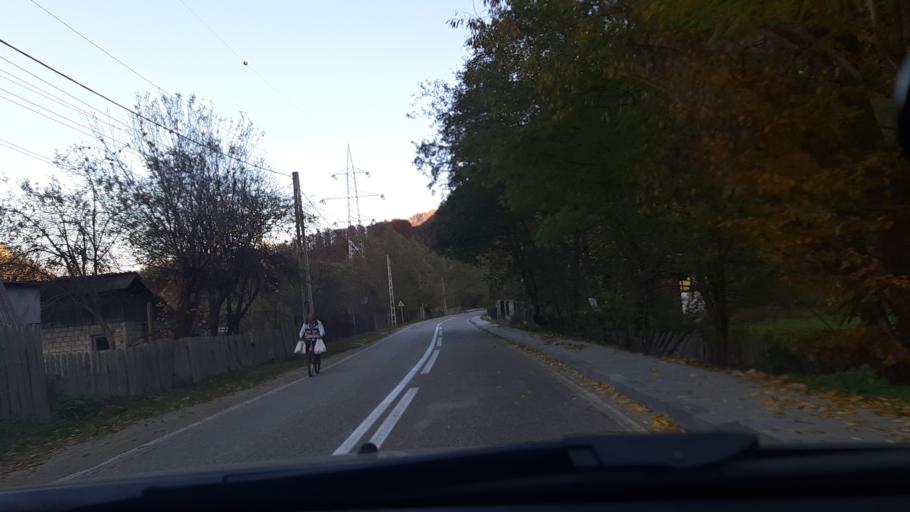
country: RO
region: Valcea
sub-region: Comuna Brezoi
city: Brezoi
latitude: 45.3490
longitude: 24.1418
